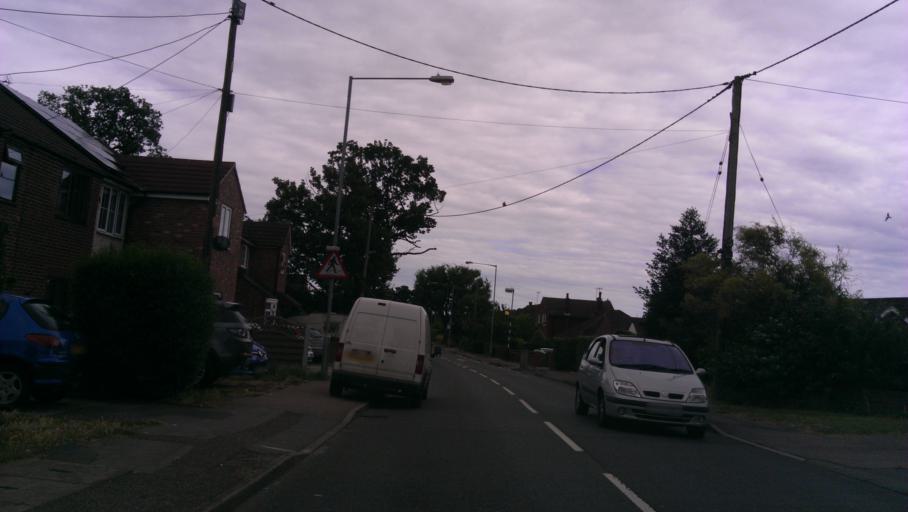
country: GB
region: England
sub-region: Essex
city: Eight Ash Green
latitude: 51.8789
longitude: 0.8374
